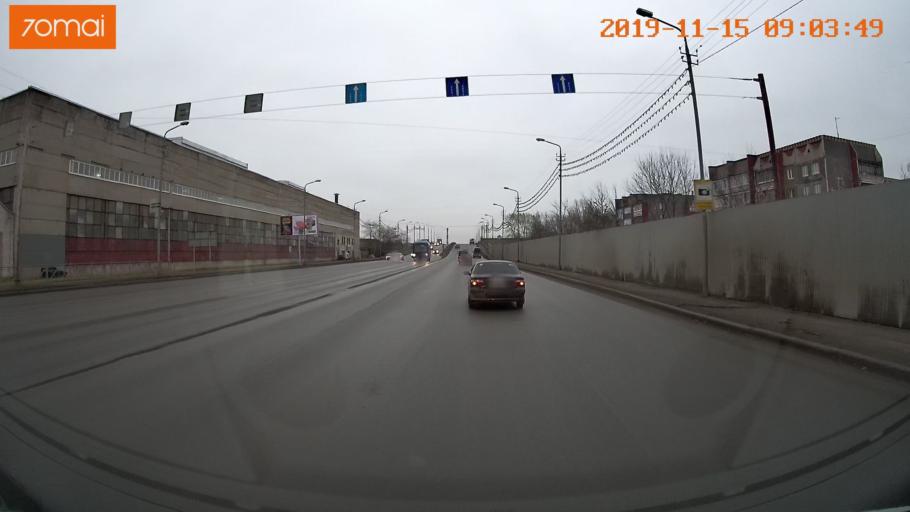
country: RU
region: Vologda
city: Cherepovets
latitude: 59.1398
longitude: 37.9193
